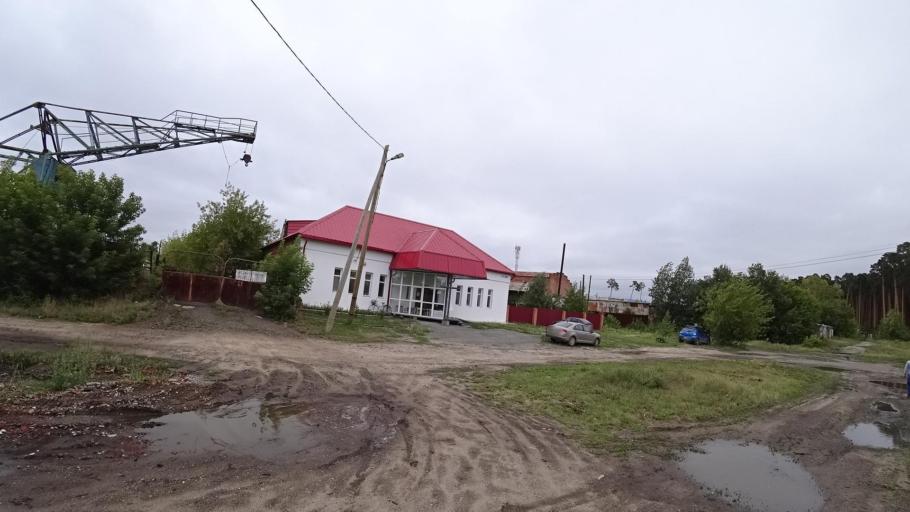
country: RU
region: Sverdlovsk
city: Kamyshlov
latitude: 56.8373
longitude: 62.7224
